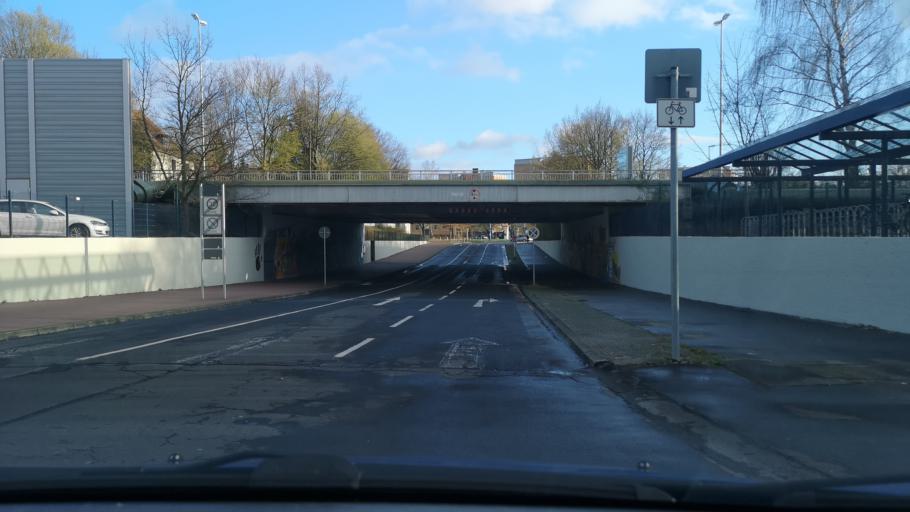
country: DE
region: Lower Saxony
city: Garbsen-Mitte
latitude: 52.4161
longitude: 9.6686
